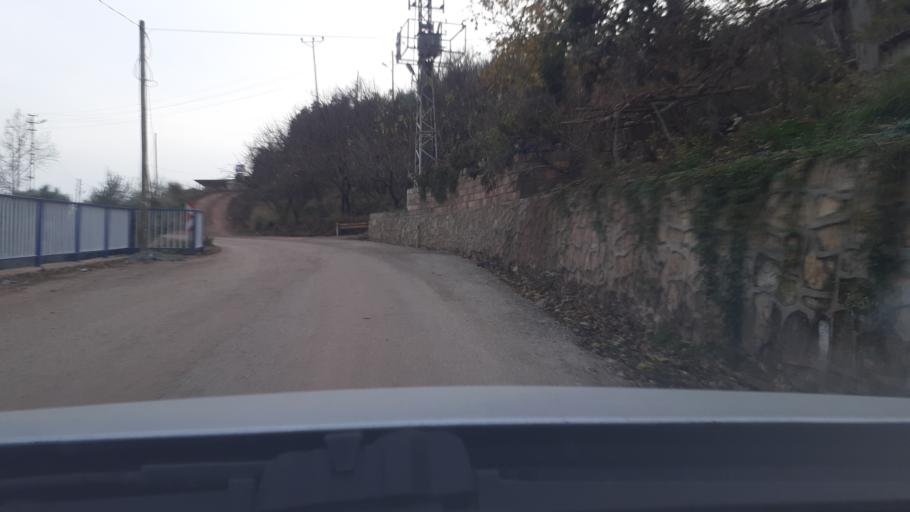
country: TR
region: Hatay
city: Kirikhan
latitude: 36.5349
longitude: 36.3143
